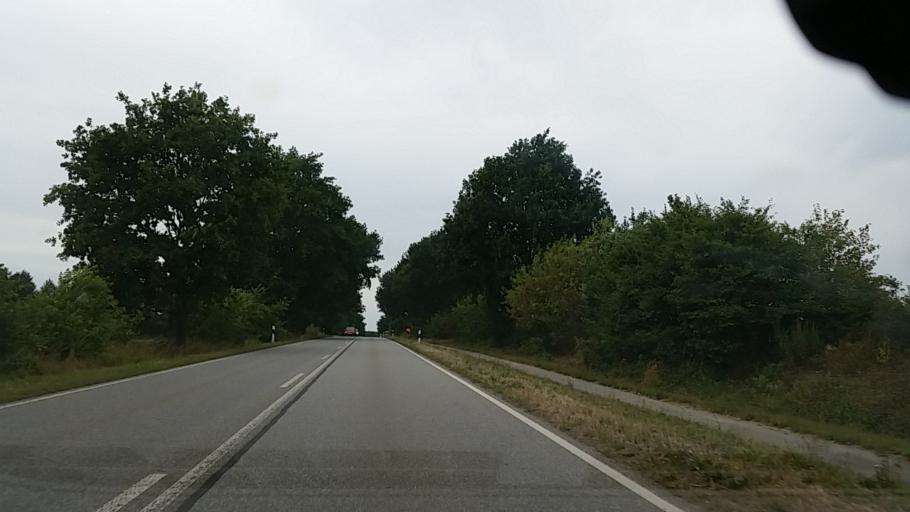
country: DE
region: Schleswig-Holstein
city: Wohltorf
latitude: 53.5296
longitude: 10.2957
